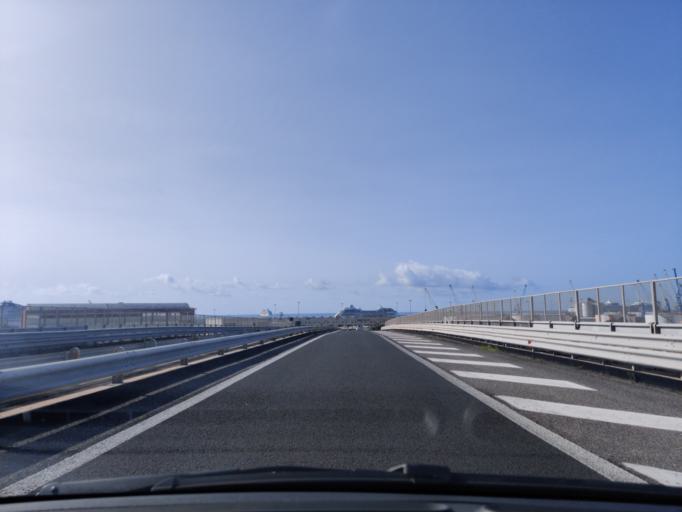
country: IT
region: Latium
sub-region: Citta metropolitana di Roma Capitale
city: Civitavecchia
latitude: 42.1047
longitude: 11.7872
